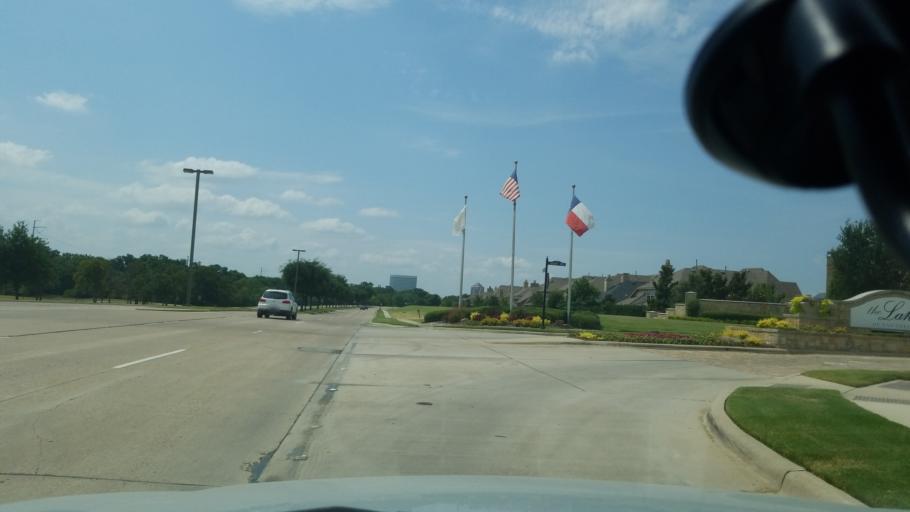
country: US
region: Texas
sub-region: Dallas County
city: Farmers Branch
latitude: 32.8804
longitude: -96.9314
